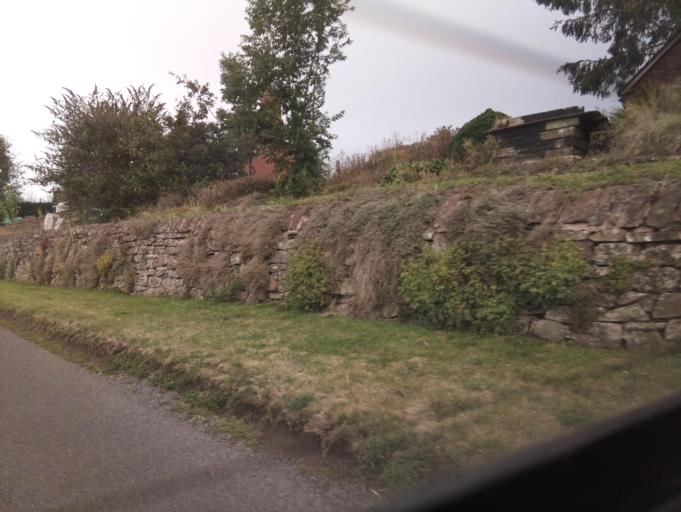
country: GB
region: England
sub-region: Shropshire
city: Woodcote
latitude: 52.7134
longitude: -2.3539
